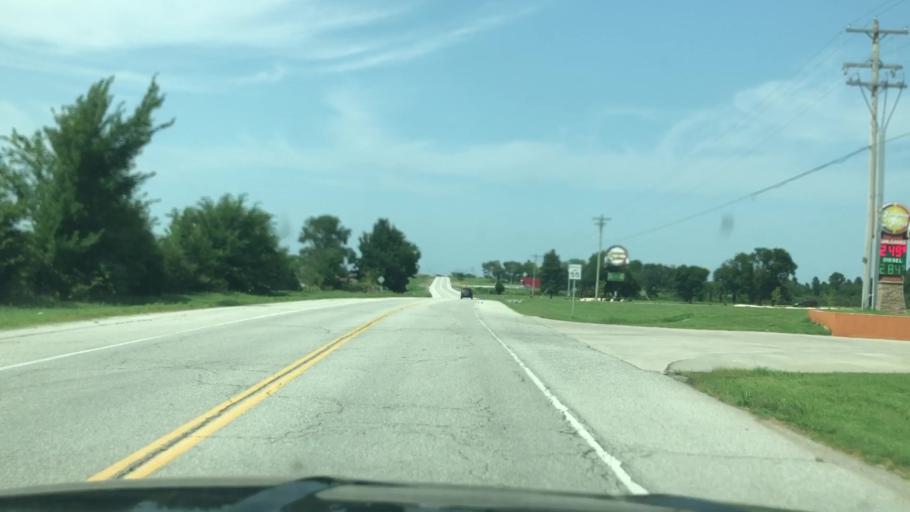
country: US
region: Oklahoma
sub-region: Ottawa County
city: Commerce
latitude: 36.9201
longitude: -94.8419
